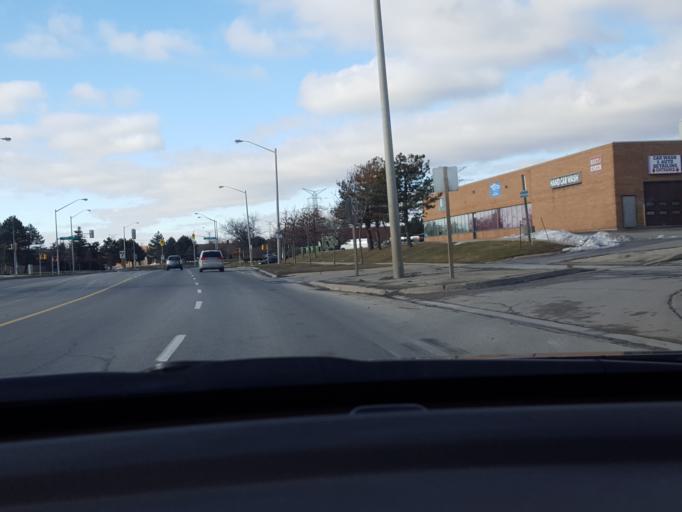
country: CA
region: Ontario
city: Concord
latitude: 43.7672
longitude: -79.5654
